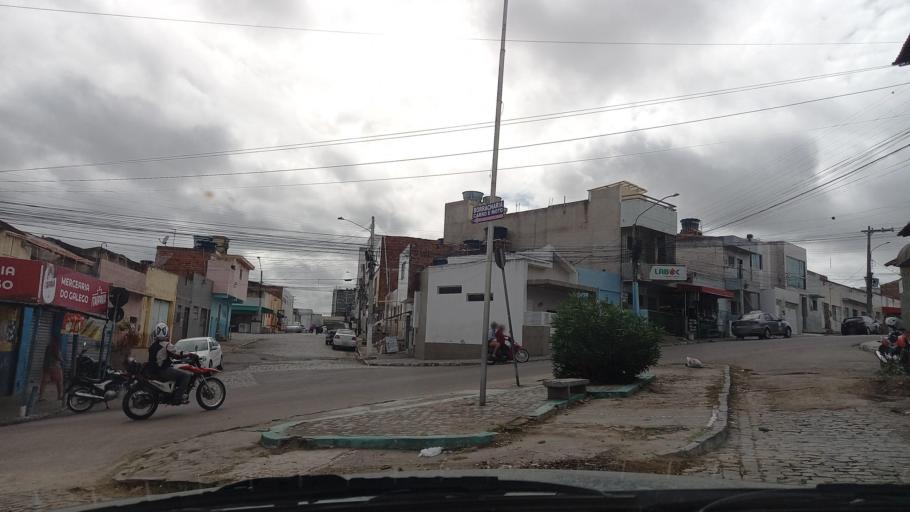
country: BR
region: Pernambuco
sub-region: Caruaru
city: Caruaru
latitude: -8.2822
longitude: -35.9768
